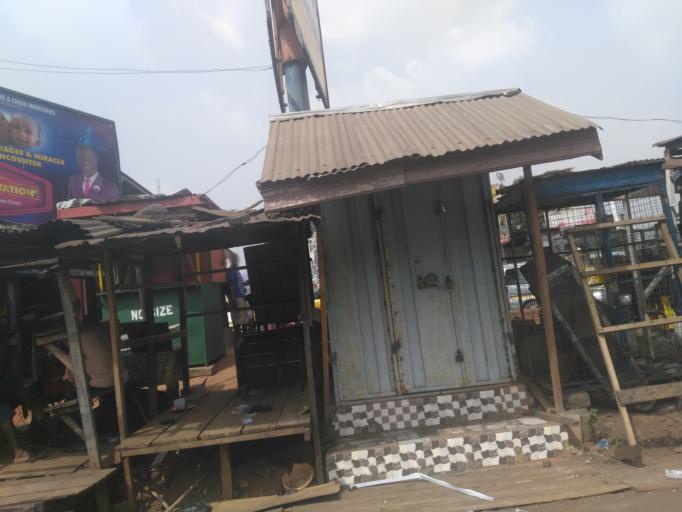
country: GH
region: Ashanti
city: Kumasi
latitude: 6.6870
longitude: -1.5745
